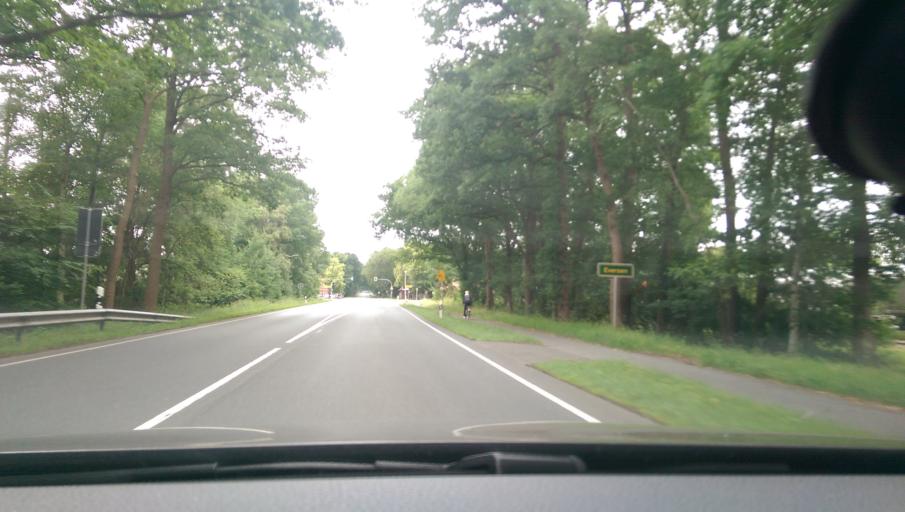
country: DE
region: Lower Saxony
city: Ahausen
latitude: 53.0473
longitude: 9.3261
